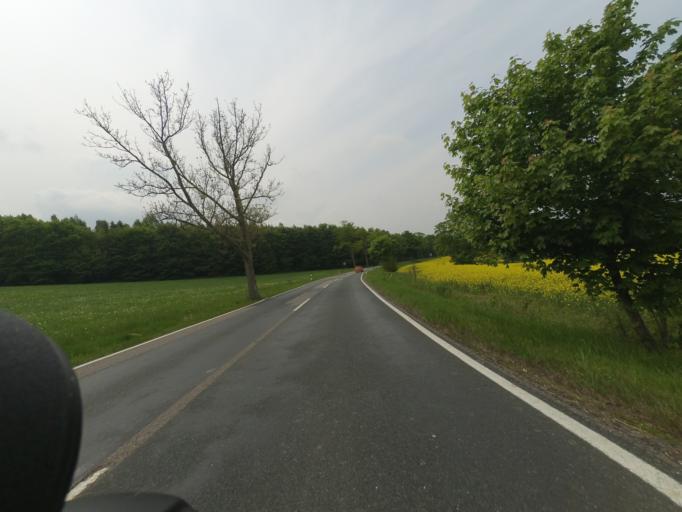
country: DE
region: Saxony
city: Grossruckerswalde
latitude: 50.6487
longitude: 13.1167
